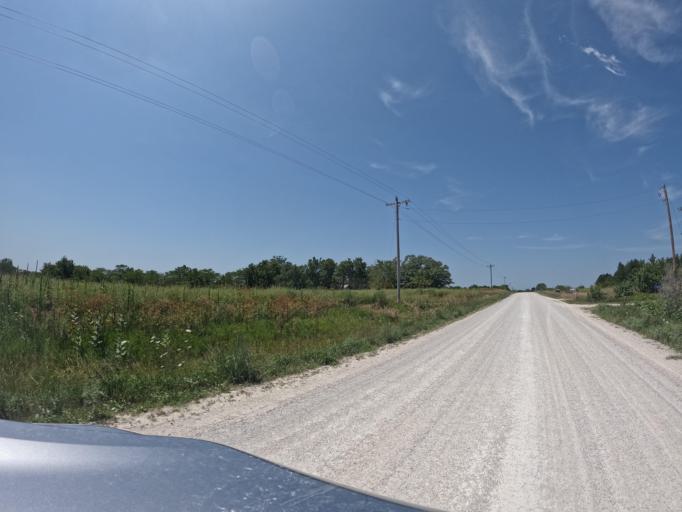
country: US
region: Iowa
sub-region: Henry County
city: Mount Pleasant
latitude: 40.9047
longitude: -91.5381
